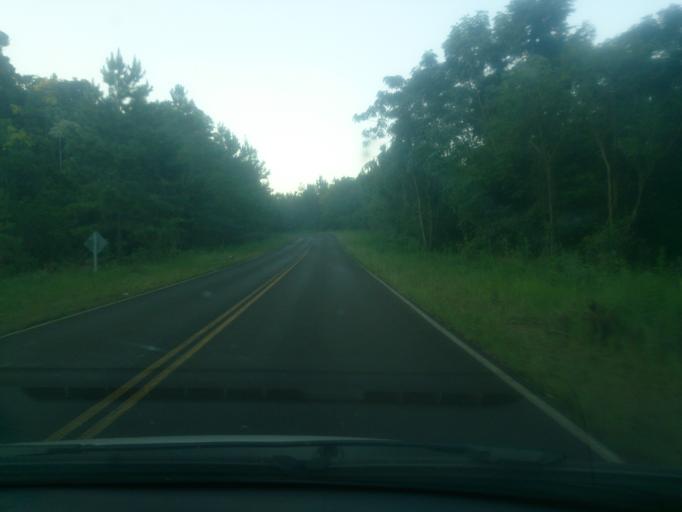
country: AR
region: Misiones
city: Panambi
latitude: -27.6756
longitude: -54.9105
